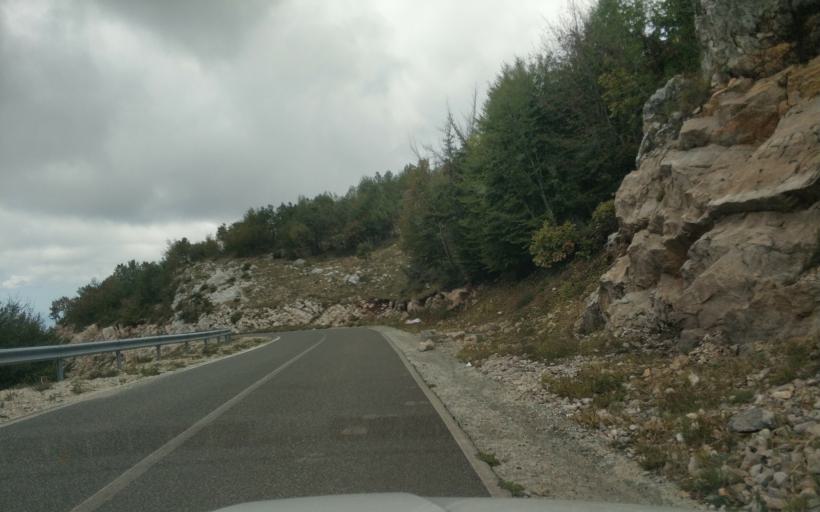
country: AL
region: Durres
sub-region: Rrethi i Krujes
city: Kruje
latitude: 41.5198
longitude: 19.8065
